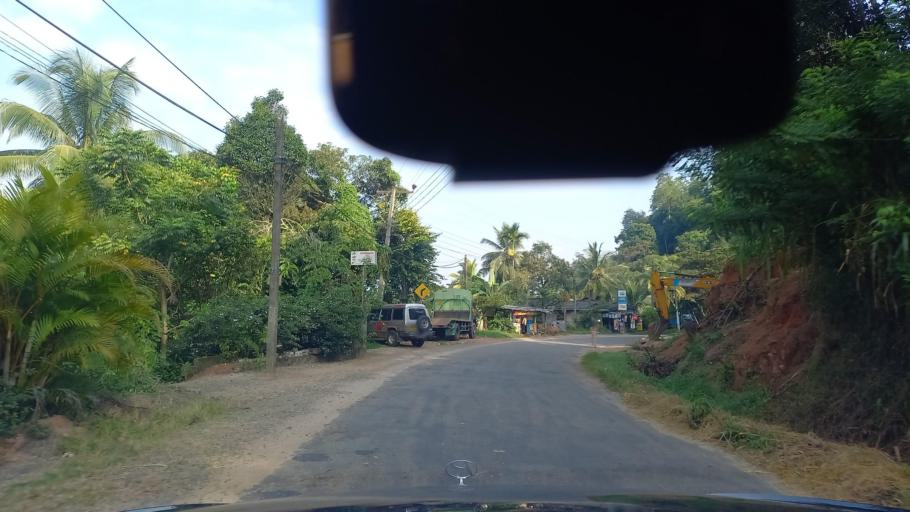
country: LK
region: Central
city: Gampola
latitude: 7.2235
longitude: 80.6053
